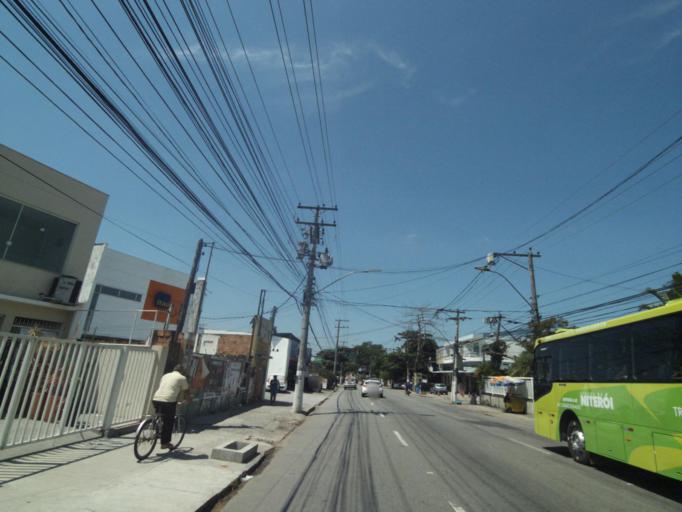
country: BR
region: Rio de Janeiro
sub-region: Niteroi
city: Niteroi
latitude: -22.9081
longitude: -43.0663
